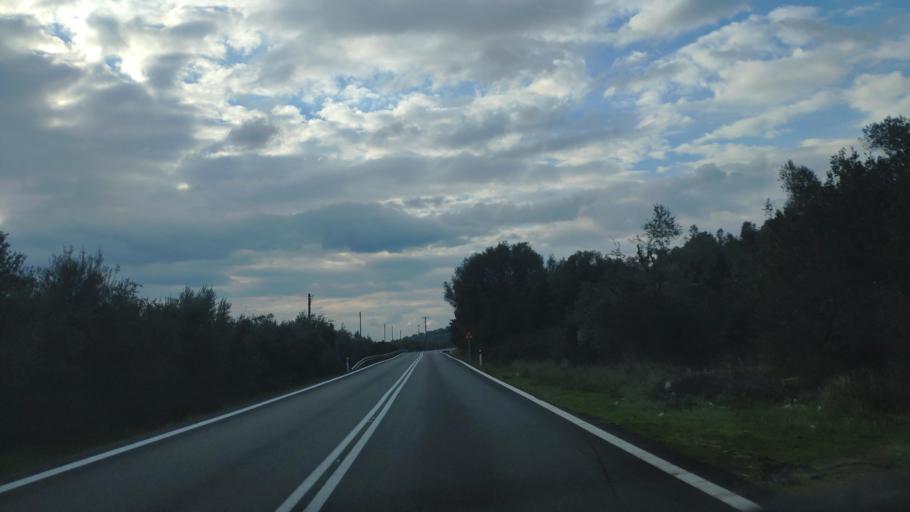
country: GR
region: Peloponnese
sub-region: Nomos Argolidos
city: Koutsopodi
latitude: 37.7464
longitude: 22.7343
